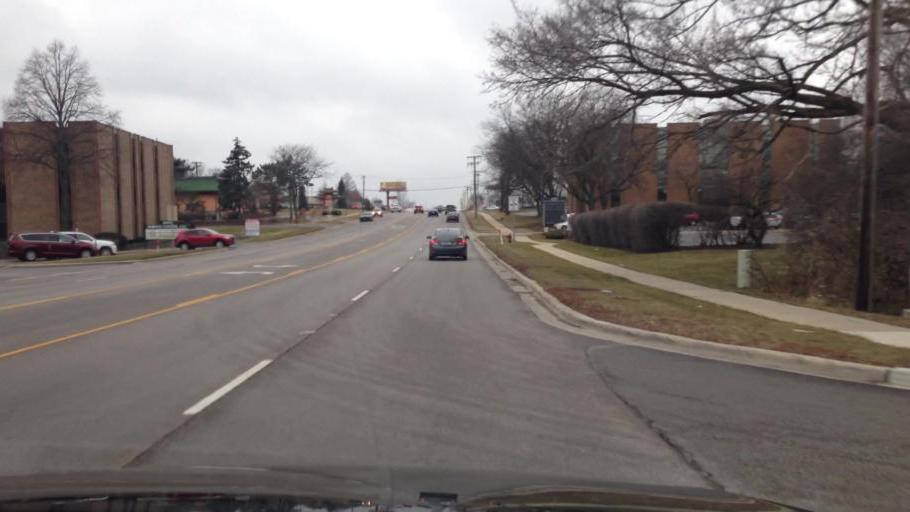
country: US
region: Illinois
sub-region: DuPage County
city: Lisle
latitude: 41.7965
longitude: -88.1103
